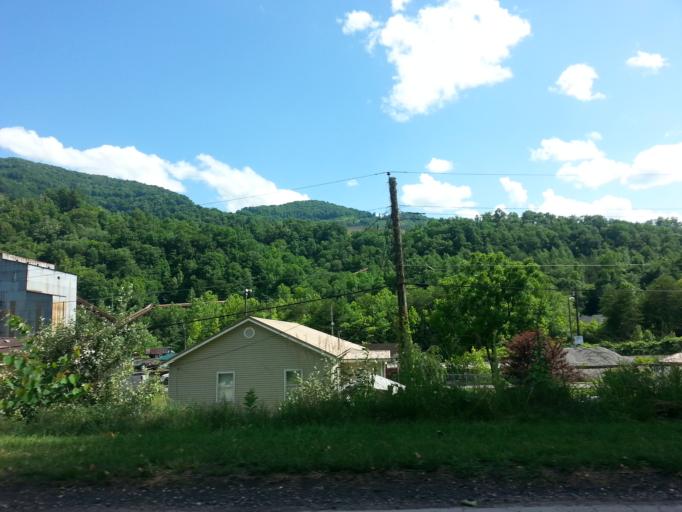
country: US
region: Kentucky
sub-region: Harlan County
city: Cumberland
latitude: 36.9445
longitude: -83.1186
